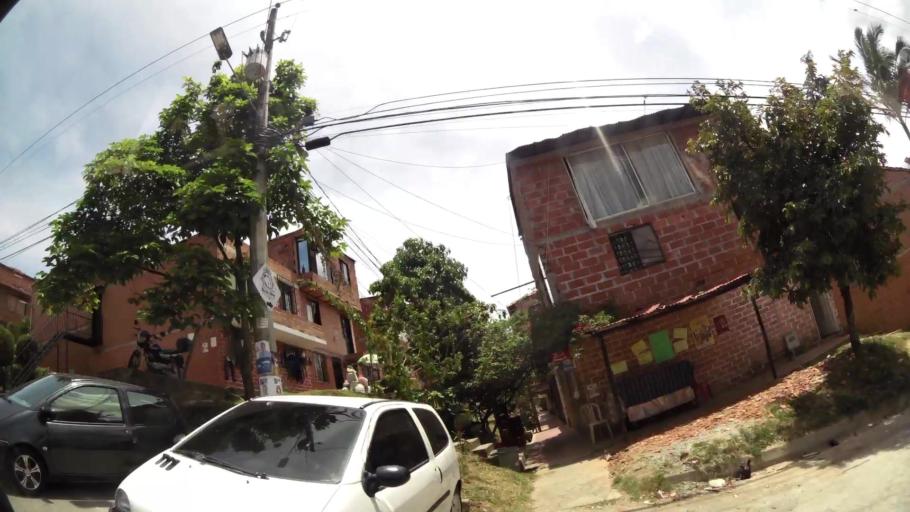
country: CO
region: Antioquia
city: Bello
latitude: 6.3512
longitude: -75.5601
